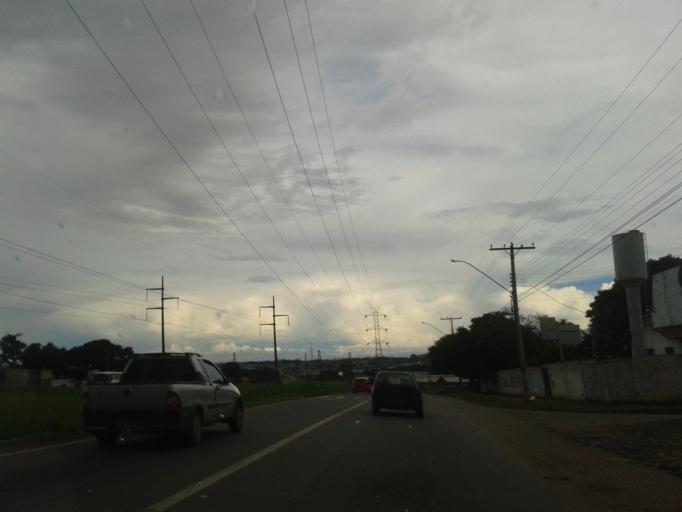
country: BR
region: Goias
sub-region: Aparecida De Goiania
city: Aparecida de Goiania
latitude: -16.7845
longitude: -49.2709
